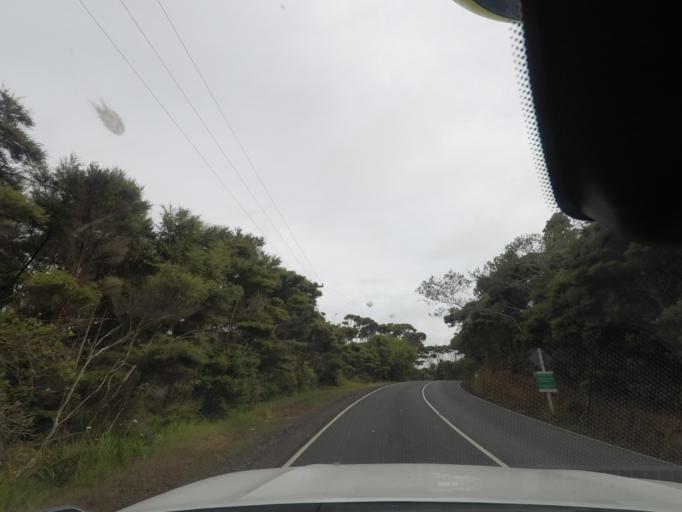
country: NZ
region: Auckland
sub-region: Auckland
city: Parakai
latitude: -36.4891
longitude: 174.2472
